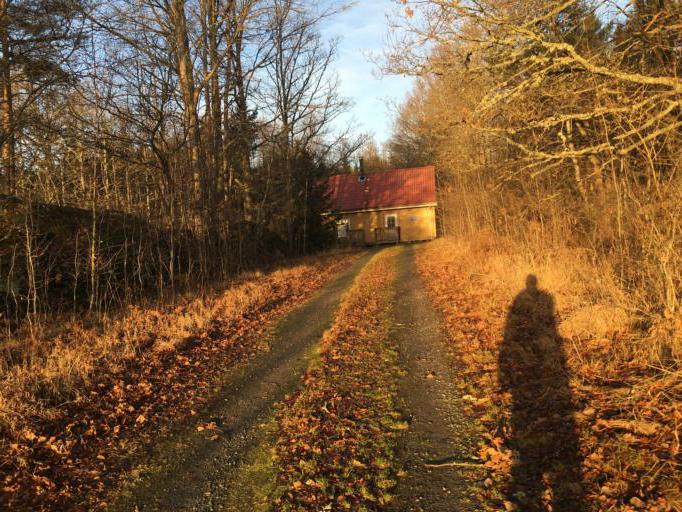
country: SE
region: Kalmar
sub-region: Vasterviks Kommun
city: Vaestervik
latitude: 57.6284
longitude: 16.5296
